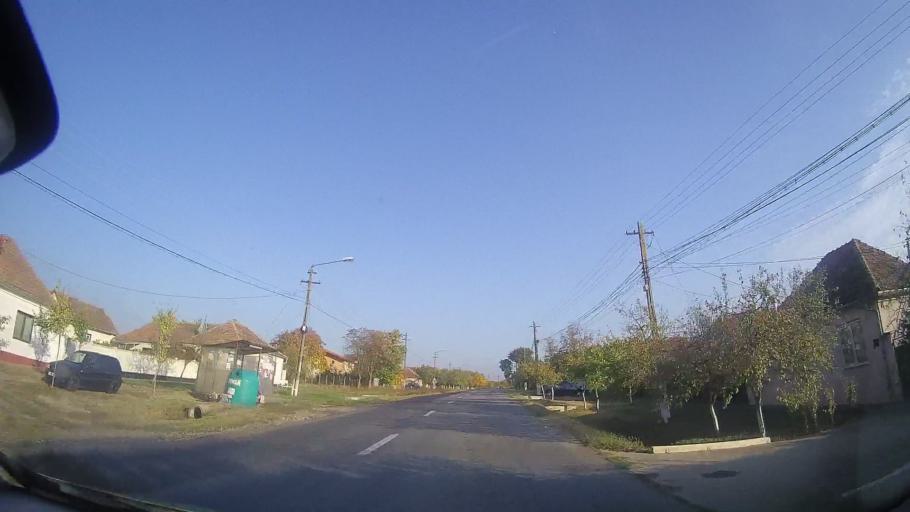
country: RO
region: Timis
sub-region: Comuna Fibis
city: Fibis
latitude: 45.9640
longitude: 21.4182
